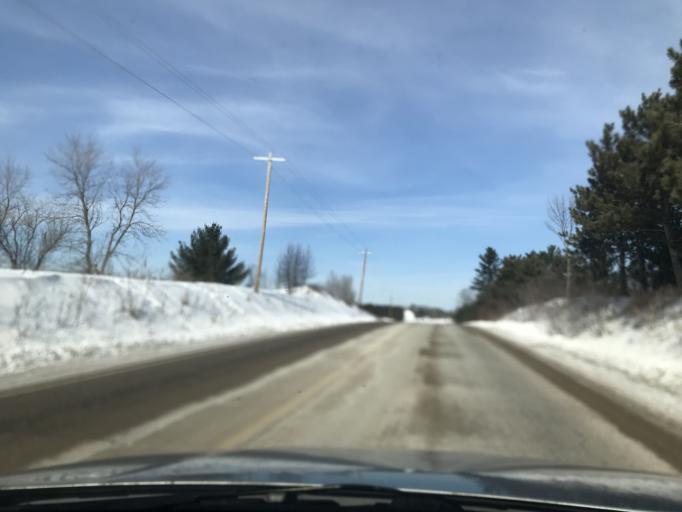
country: US
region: Wisconsin
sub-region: Oconto County
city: Oconto Falls
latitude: 45.1431
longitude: -88.1771
